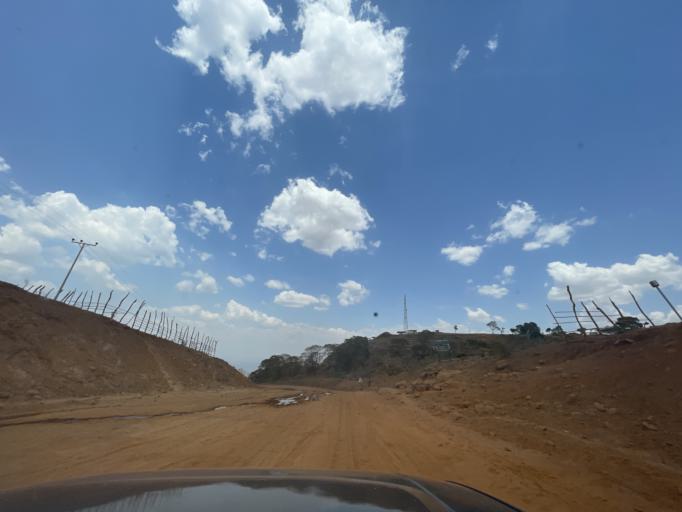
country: ET
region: Amhara
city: Bure
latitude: 10.1490
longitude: 36.9457
